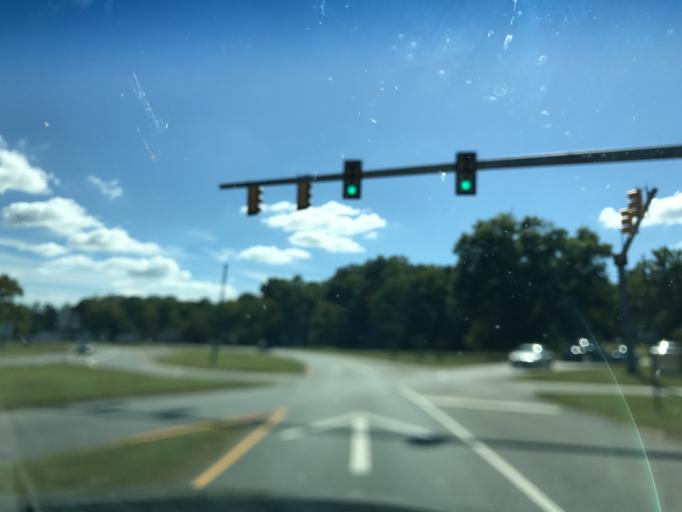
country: US
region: Virginia
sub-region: Essex County
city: Tappahannock
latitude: 37.8964
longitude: -76.8718
